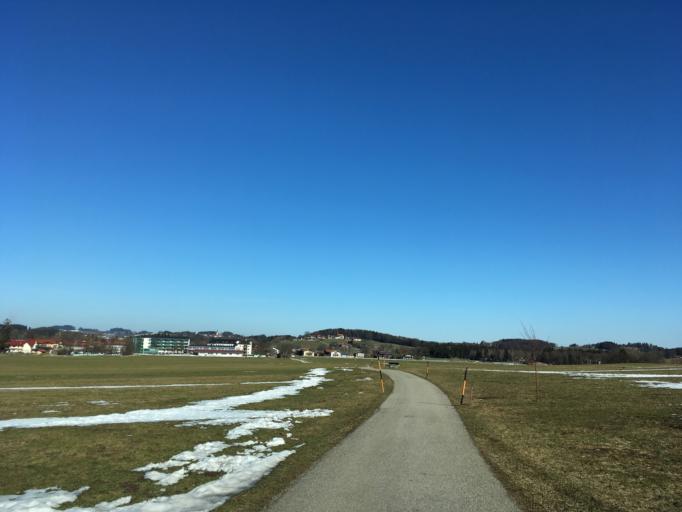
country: DE
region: Bavaria
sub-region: Upper Bavaria
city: Aschau im Chiemgau
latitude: 47.7768
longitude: 12.3301
